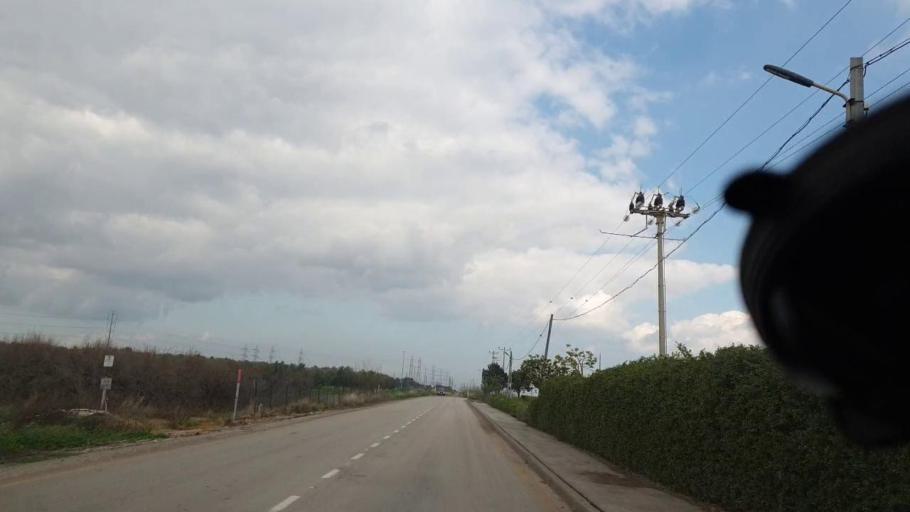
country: IL
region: Haifa
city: Rekhasim
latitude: 32.7532
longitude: 35.0865
